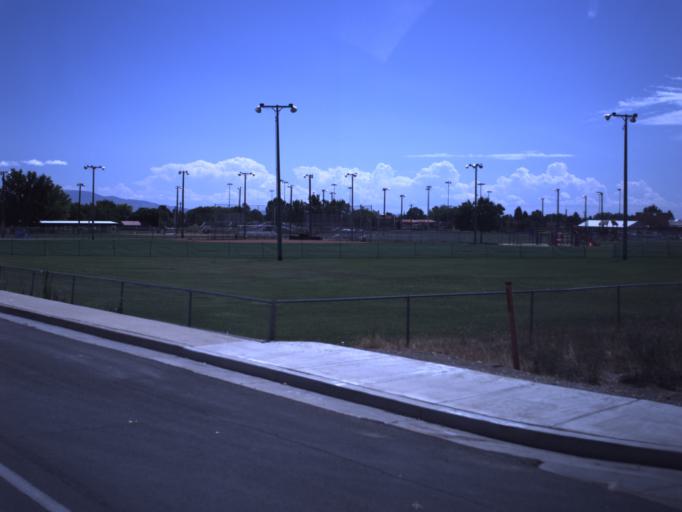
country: US
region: Utah
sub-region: Uintah County
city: Vernal
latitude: 40.4627
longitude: -109.5506
